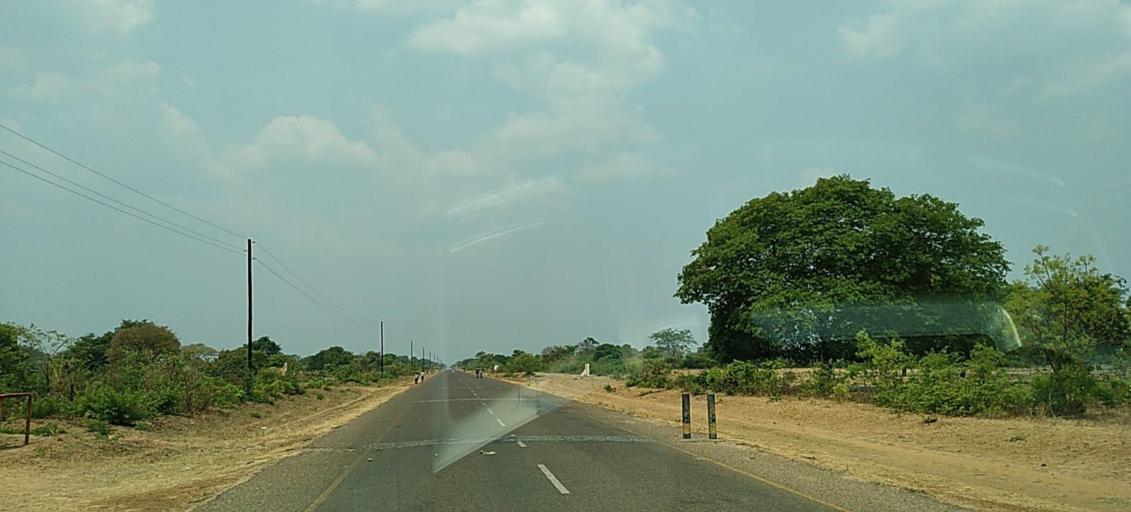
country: ZM
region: North-Western
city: Zambezi
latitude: -13.5513
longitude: 23.1276
